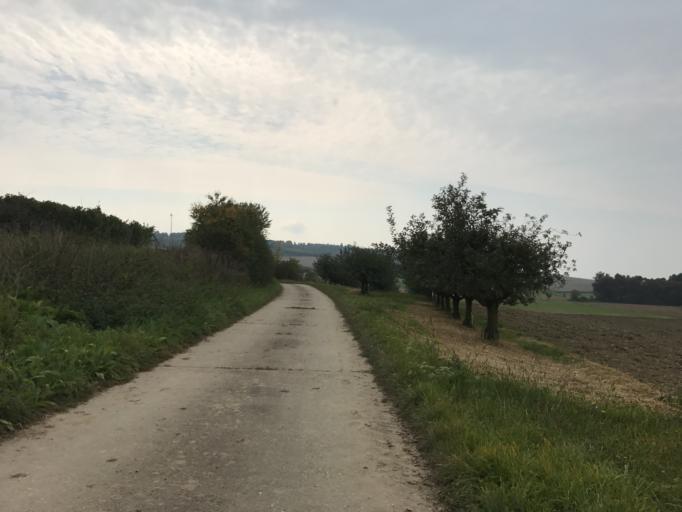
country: DE
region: Rheinland-Pfalz
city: Klein-Winternheim
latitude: 49.9292
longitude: 8.2213
